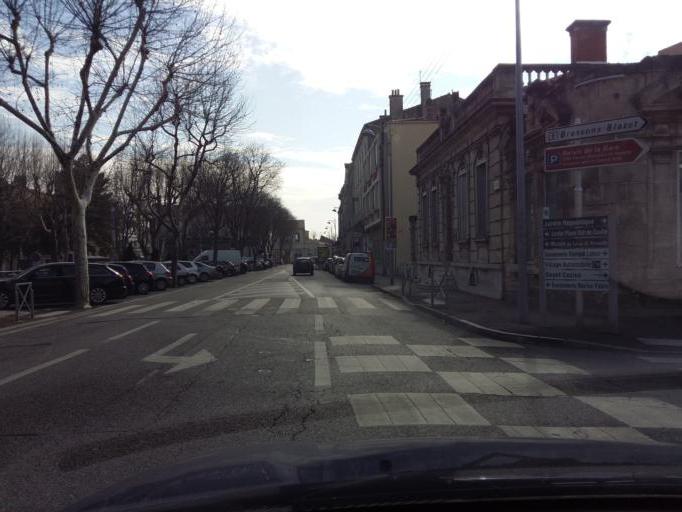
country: FR
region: Provence-Alpes-Cote d'Azur
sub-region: Departement des Bouches-du-Rhone
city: Salon-de-Provence
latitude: 43.6419
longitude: 5.0945
